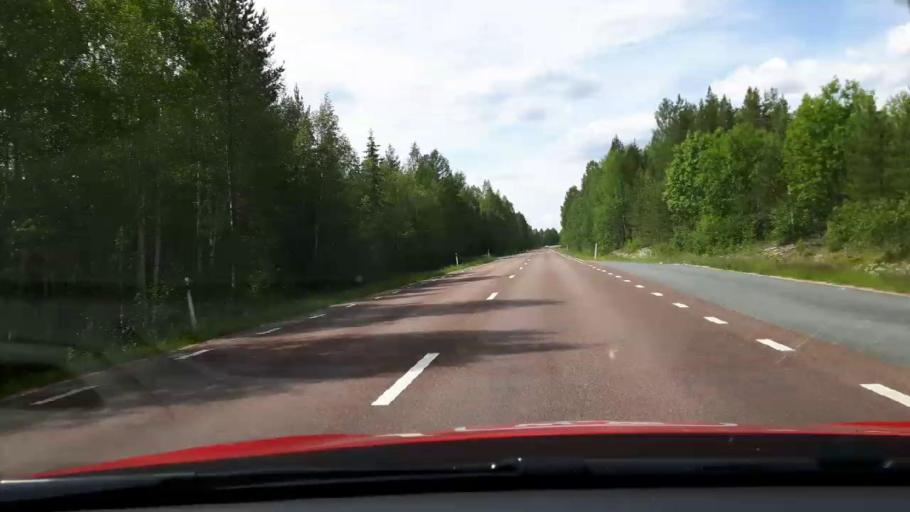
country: SE
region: Jaemtland
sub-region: Harjedalens Kommun
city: Sveg
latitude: 62.0463
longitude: 14.8220
